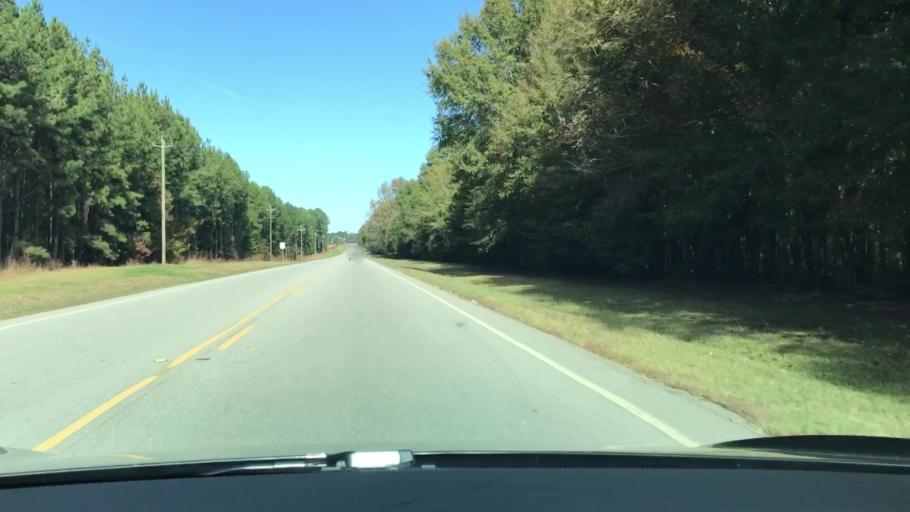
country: US
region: Georgia
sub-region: Warren County
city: Firing Range
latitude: 33.4419
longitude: -82.6922
